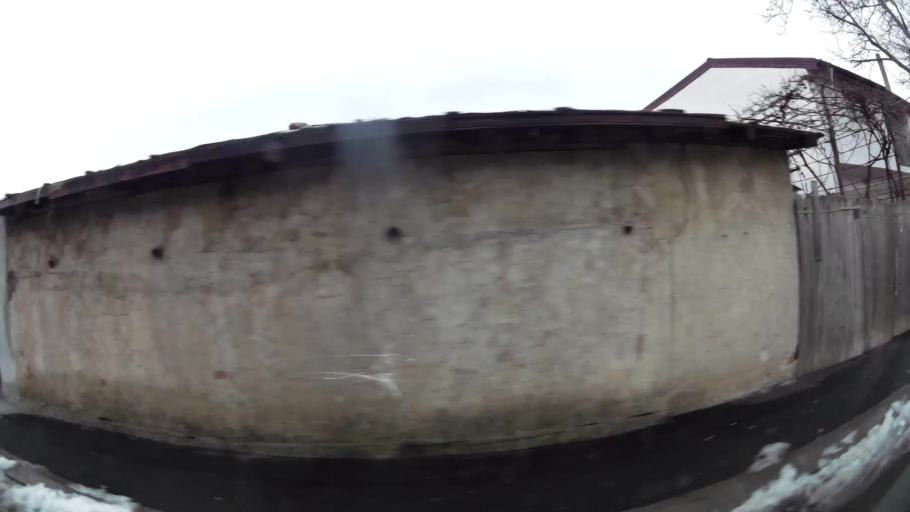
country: RO
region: Ilfov
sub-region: Voluntari City
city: Voluntari
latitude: 44.4827
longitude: 26.1855
